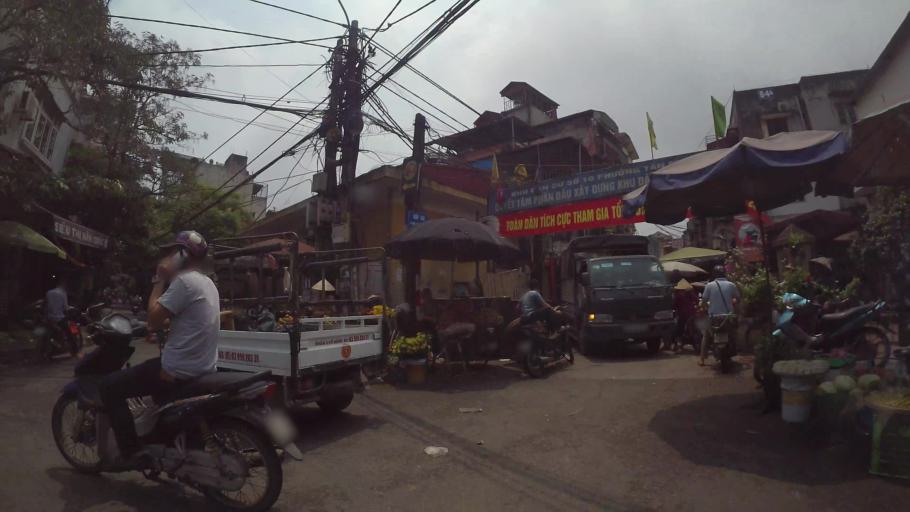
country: VN
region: Ha Noi
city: Hai BaTrung
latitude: 20.9802
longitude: 105.8497
